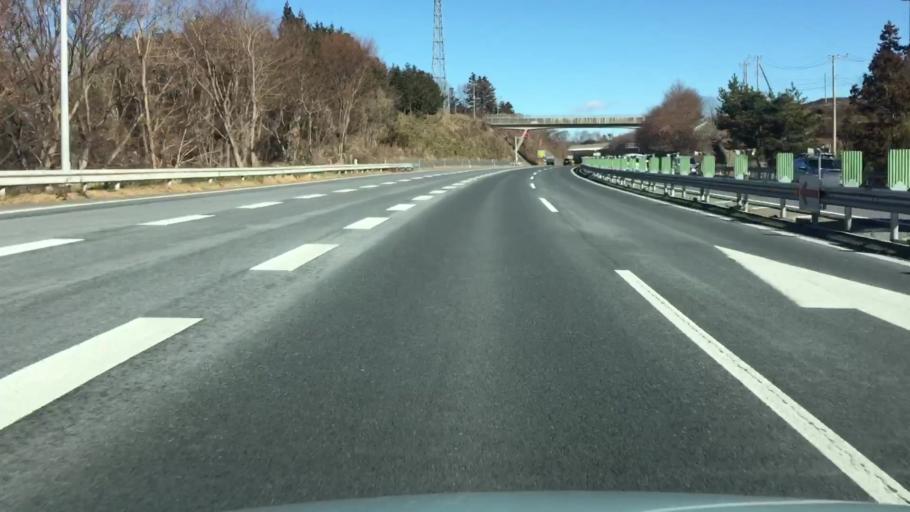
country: JP
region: Gunma
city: Shibukawa
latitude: 36.5402
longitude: 139.0492
